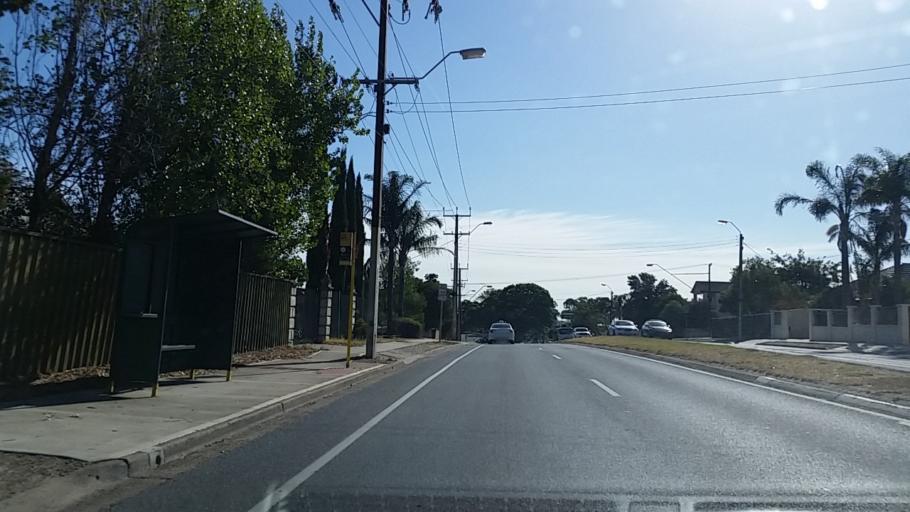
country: AU
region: South Australia
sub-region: Campbelltown
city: Athelstone
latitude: -34.8527
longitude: 138.7061
